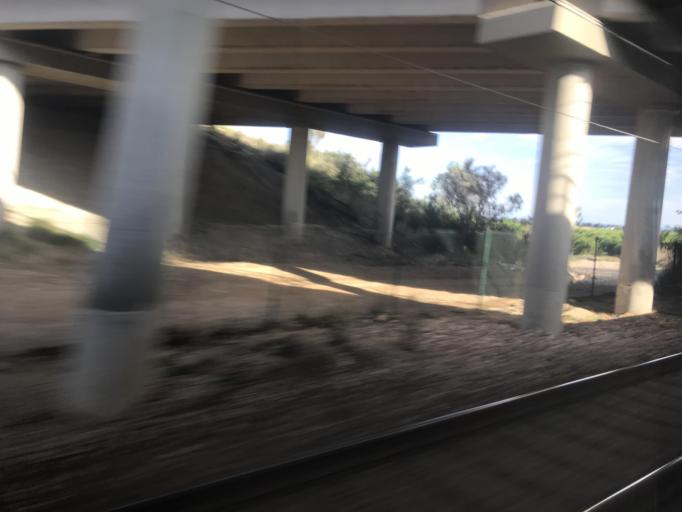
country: ES
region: Catalonia
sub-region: Provincia de Tarragona
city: Ulldecona
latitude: 40.5555
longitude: 0.4251
